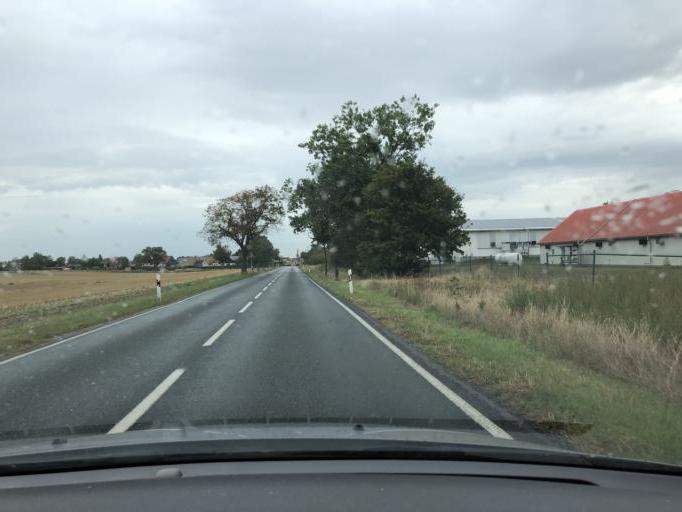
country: DE
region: Saxony-Anhalt
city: Wulfen
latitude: 51.8120
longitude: 11.8977
